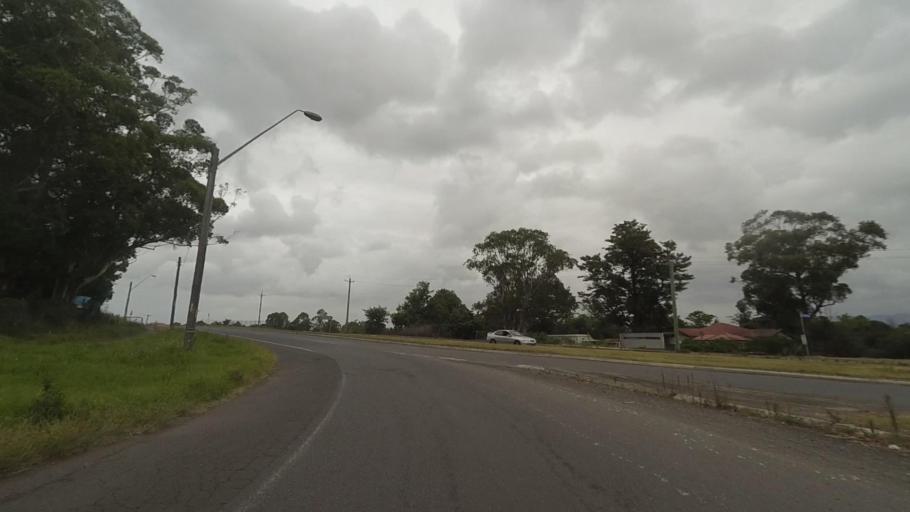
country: AU
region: New South Wales
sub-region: Wollongong
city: Berkeley
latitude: -34.4686
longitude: 150.8271
